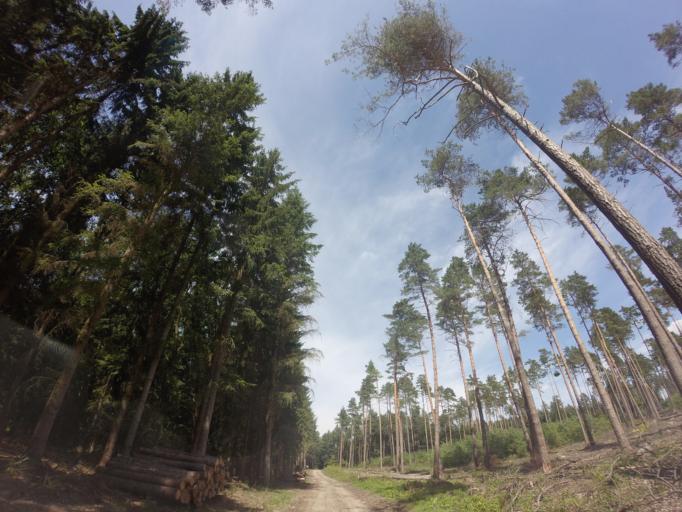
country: PL
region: West Pomeranian Voivodeship
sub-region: Powiat choszczenski
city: Recz
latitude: 53.3222
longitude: 15.5311
